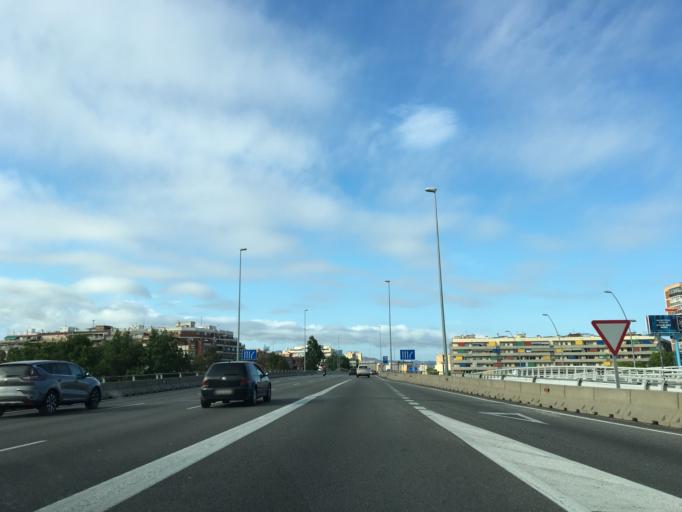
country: ES
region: Catalonia
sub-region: Provincia de Barcelona
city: Sant Adria de Besos
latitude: 41.4261
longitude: 2.2185
